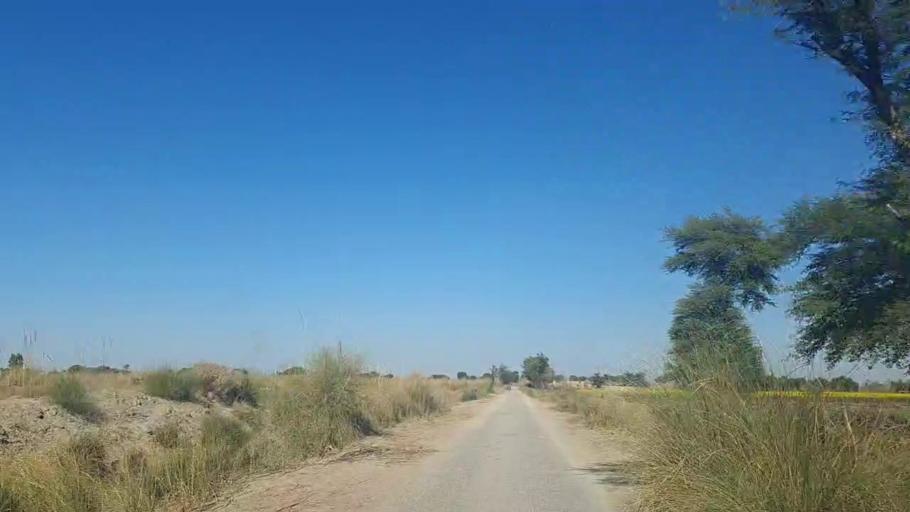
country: PK
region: Sindh
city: Khadro
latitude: 26.2124
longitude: 68.8601
